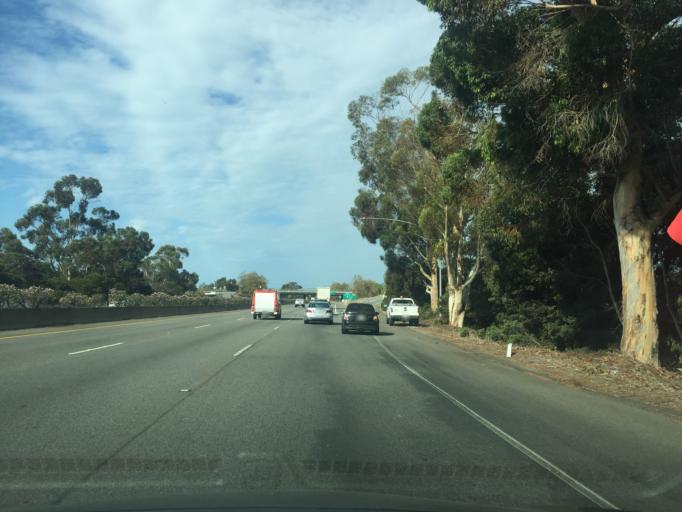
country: US
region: California
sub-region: Santa Barbara County
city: Goleta
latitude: 34.4422
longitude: -119.7843
